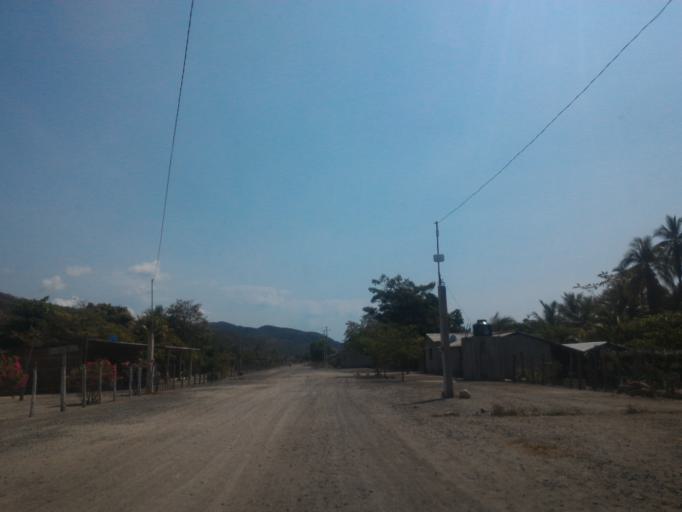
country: MX
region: Michoacan
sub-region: Coalcoman de Vazquez Pallares
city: Coalcoman de Vazquez Pallares
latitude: 18.2735
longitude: -103.3457
